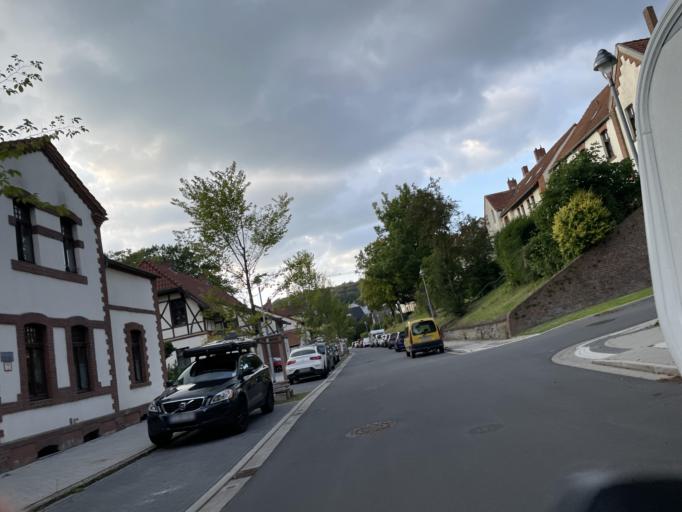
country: DE
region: North Rhine-Westphalia
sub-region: Regierungsbezirk Dusseldorf
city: Velbert
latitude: 51.4009
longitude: 7.0567
